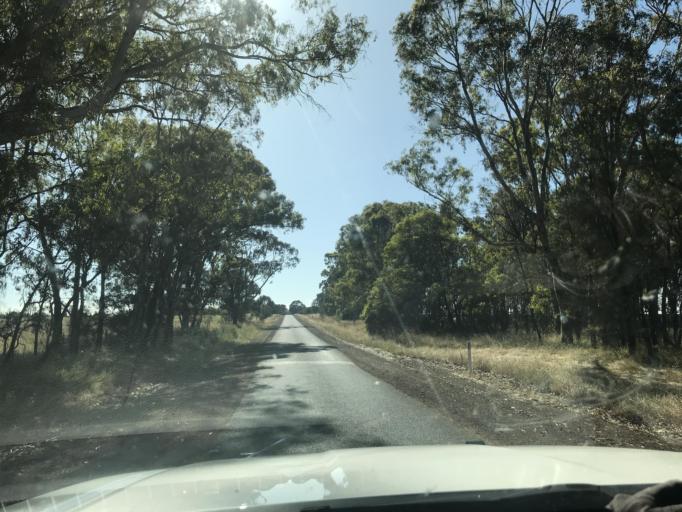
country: AU
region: Victoria
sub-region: Horsham
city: Horsham
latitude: -37.0062
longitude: 141.6326
